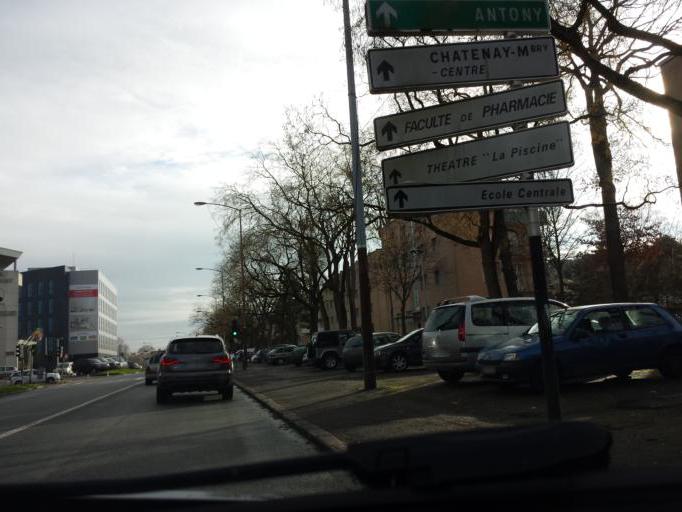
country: FR
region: Ile-de-France
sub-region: Departement des Hauts-de-Seine
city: Chatenay-Malabry
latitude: 48.7676
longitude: 2.2527
